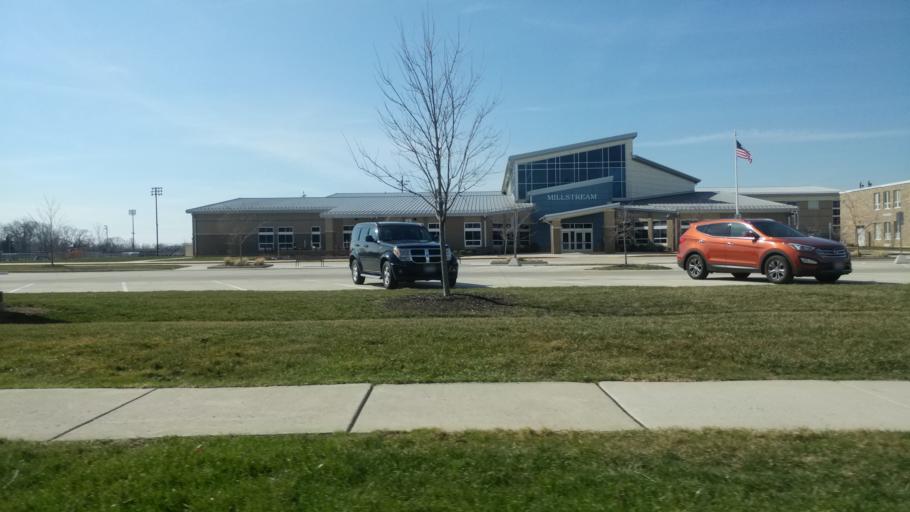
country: US
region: Ohio
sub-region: Hancock County
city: Findlay
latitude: 41.0545
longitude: -83.6646
